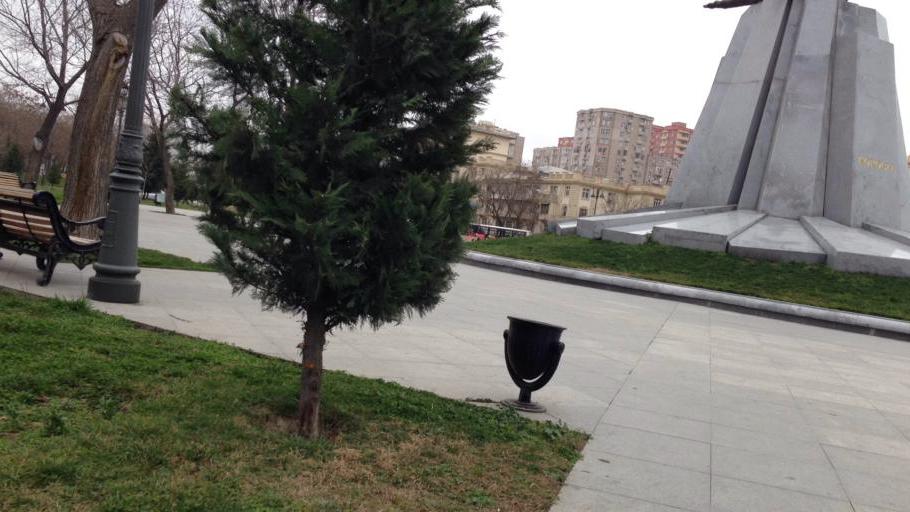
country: AZ
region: Baki
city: Baku
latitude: 40.3919
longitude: 49.8422
